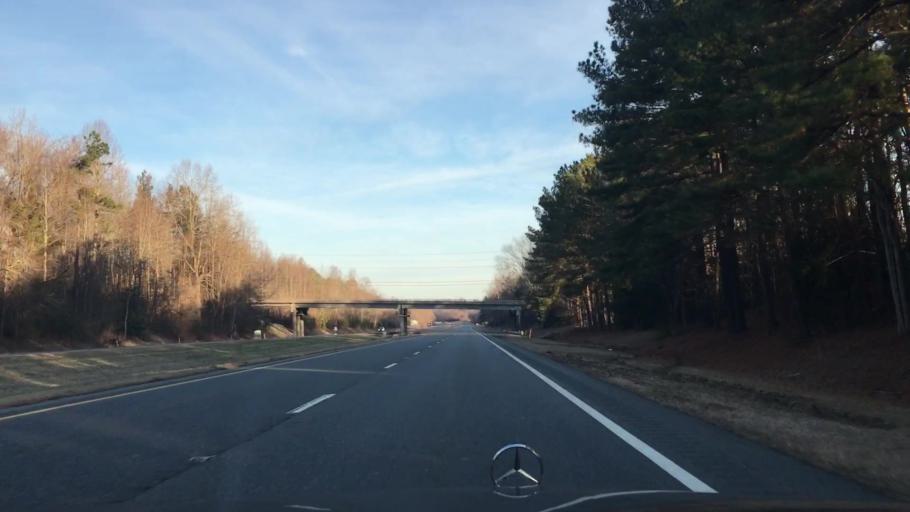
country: US
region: North Carolina
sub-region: Guilford County
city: Pleasant Garden
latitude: 36.0117
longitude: -79.7598
